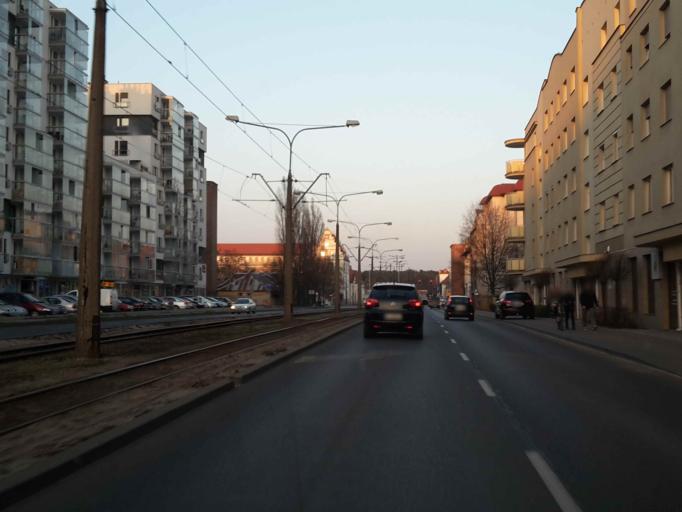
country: PL
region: Kujawsko-Pomorskie
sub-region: Torun
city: Torun
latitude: 53.0138
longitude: 18.5763
